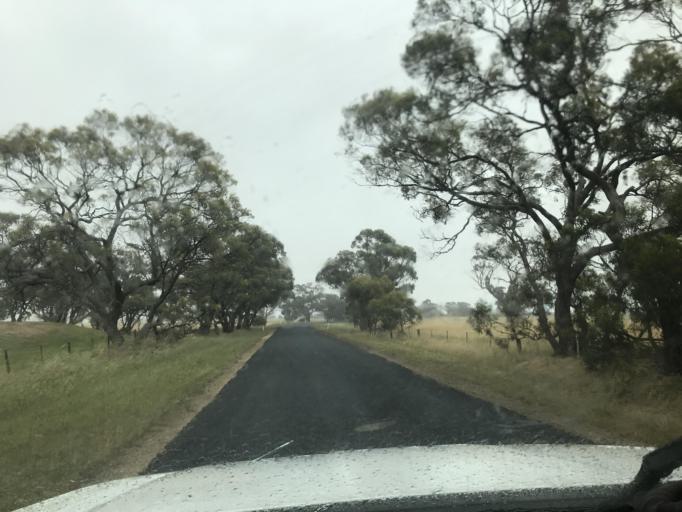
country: AU
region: South Australia
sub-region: Tatiara
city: Bordertown
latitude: -36.3271
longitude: 141.2089
